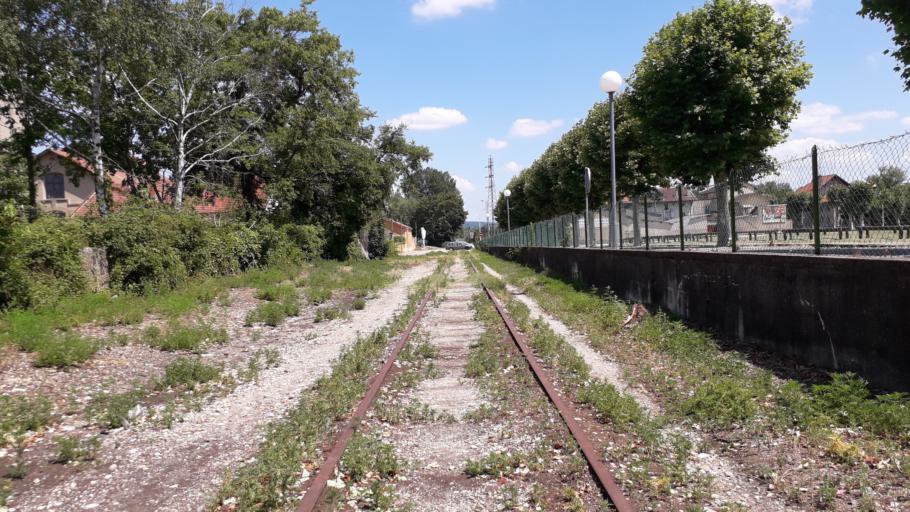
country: FR
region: Rhone-Alpes
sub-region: Departement de l'Isere
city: Charvieu-Chavagneux
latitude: 45.7469
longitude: 5.1654
